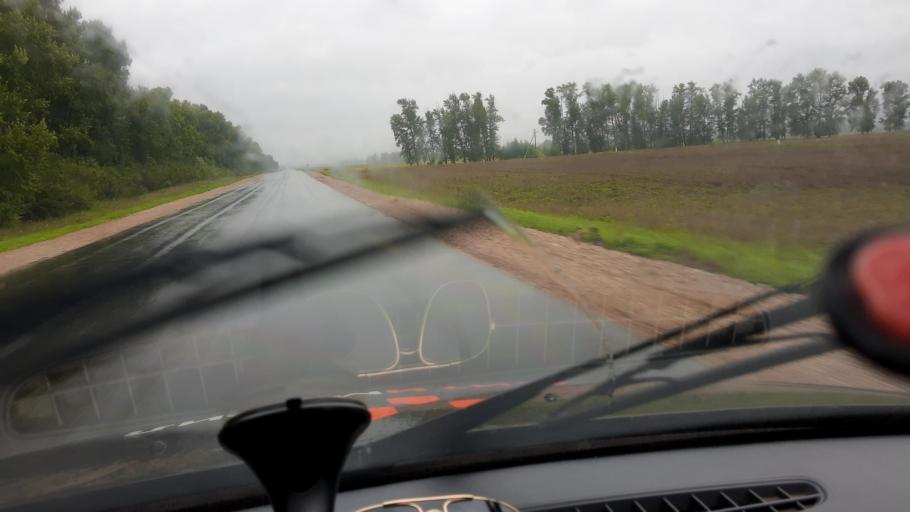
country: RU
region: Bashkortostan
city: Karmaskaly
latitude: 53.9614
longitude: 56.3995
